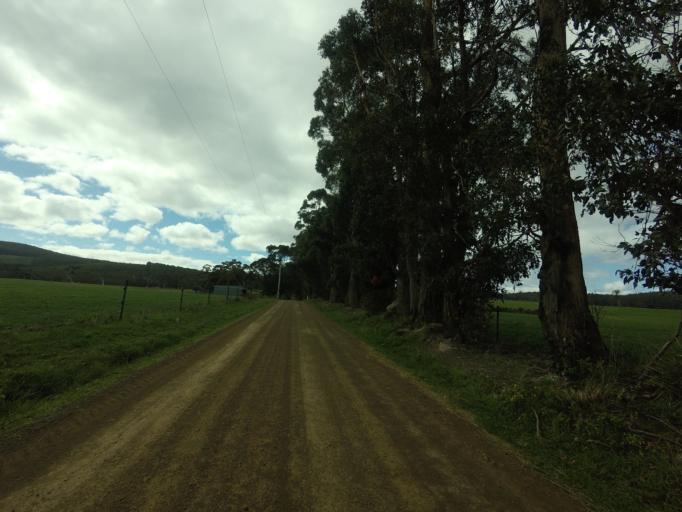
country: AU
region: Tasmania
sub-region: Huon Valley
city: Geeveston
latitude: -43.4304
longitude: 146.9913
